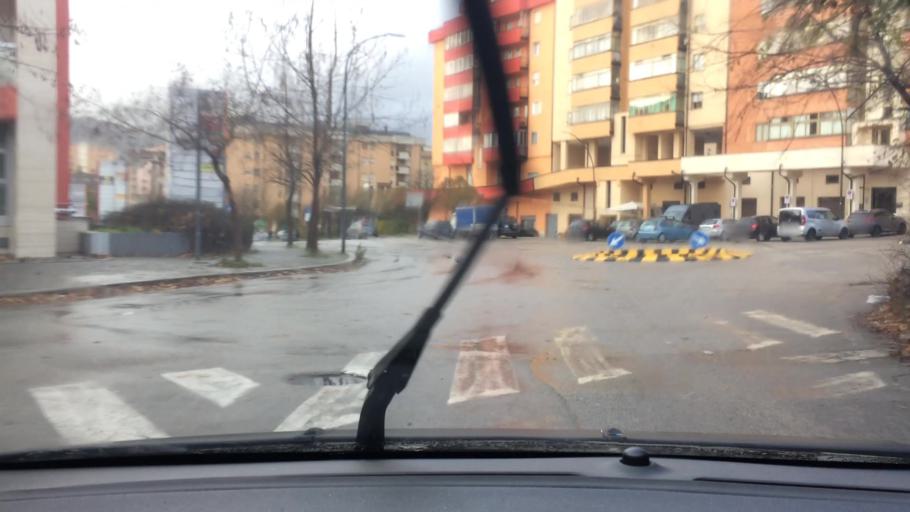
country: IT
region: Basilicate
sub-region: Provincia di Potenza
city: Potenza
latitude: 40.6428
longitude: 15.7911
